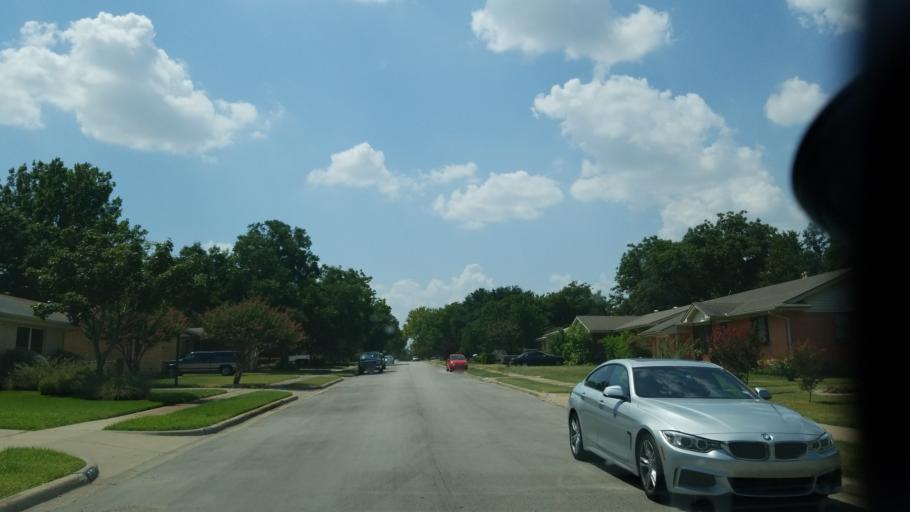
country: US
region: Texas
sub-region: Dallas County
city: Garland
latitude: 32.9278
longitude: -96.6415
